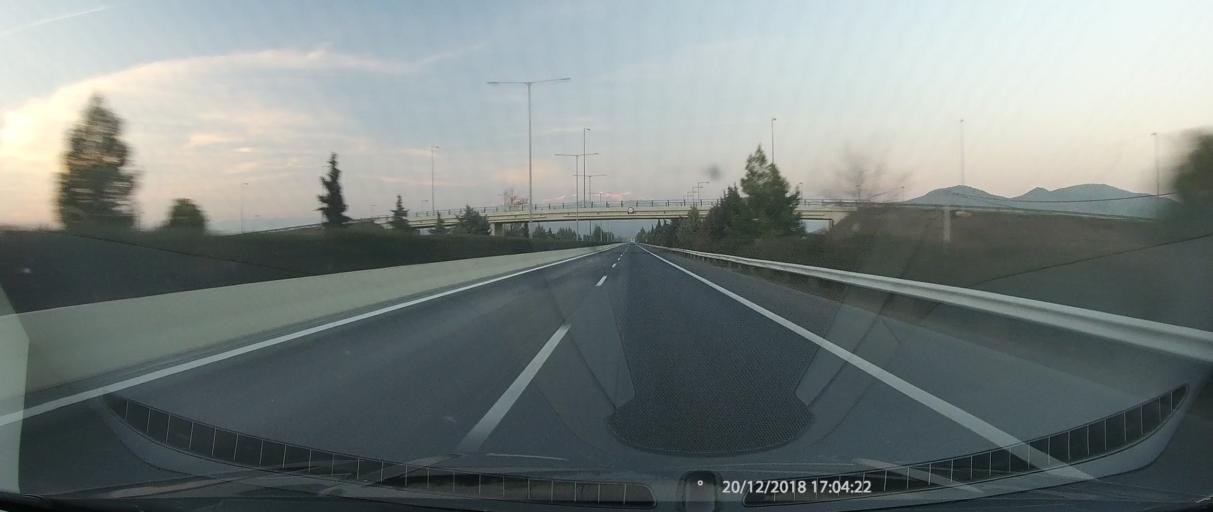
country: GR
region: Thessaly
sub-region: Nomos Larisis
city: Makrychori
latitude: 39.7162
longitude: 22.4826
